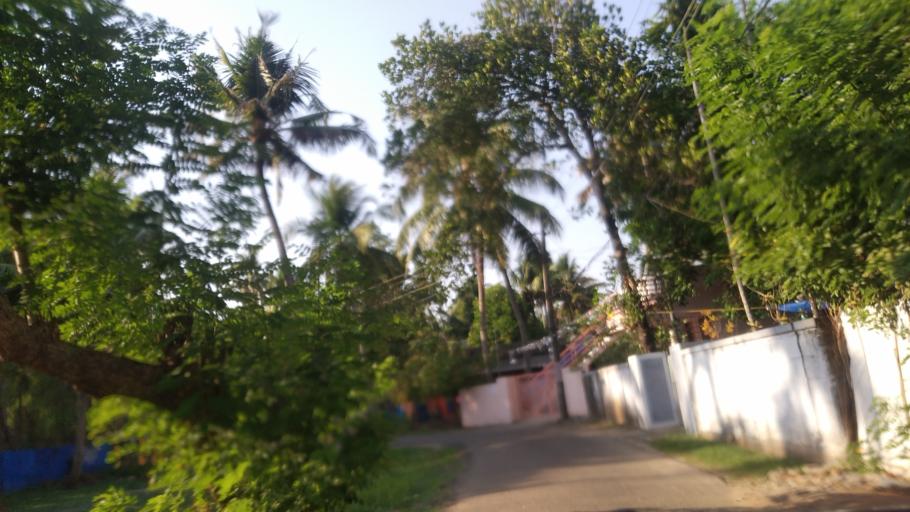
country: IN
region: Kerala
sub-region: Thrissur District
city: Kodungallur
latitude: 10.1311
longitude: 76.2023
